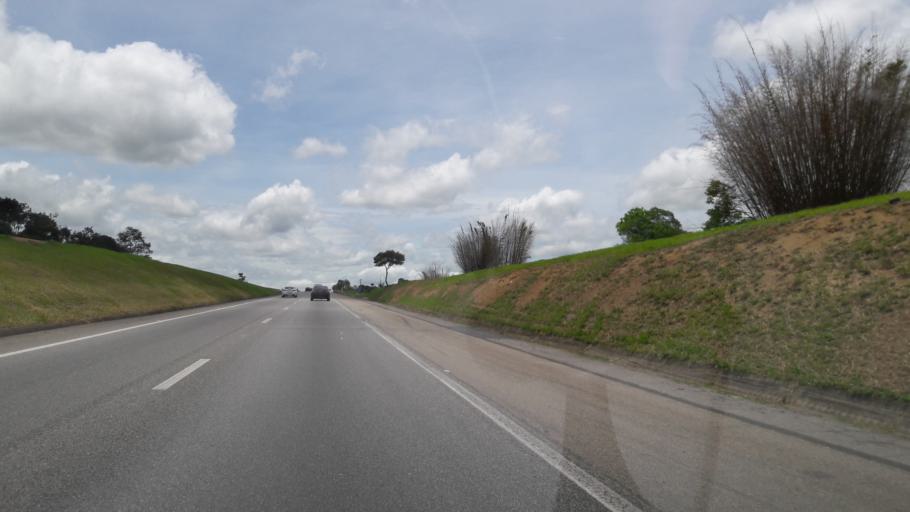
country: BR
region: Sao Paulo
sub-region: Sorocaba
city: Sorocaba
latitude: -23.3720
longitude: -47.4436
